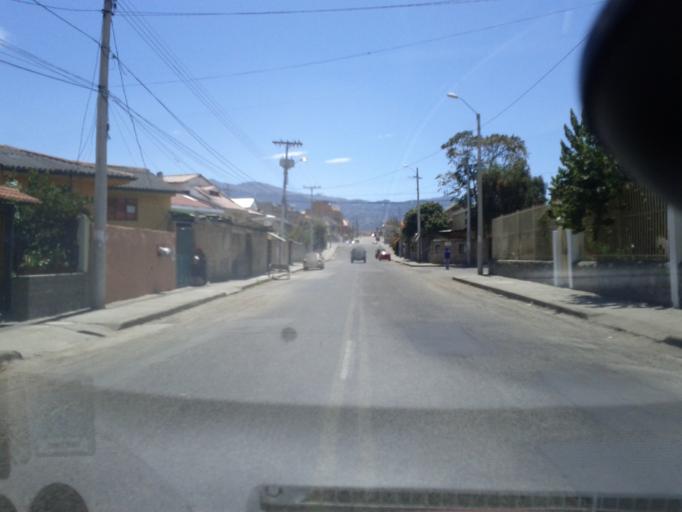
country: EC
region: Azuay
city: Cuenca
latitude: -2.9075
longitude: -79.0151
